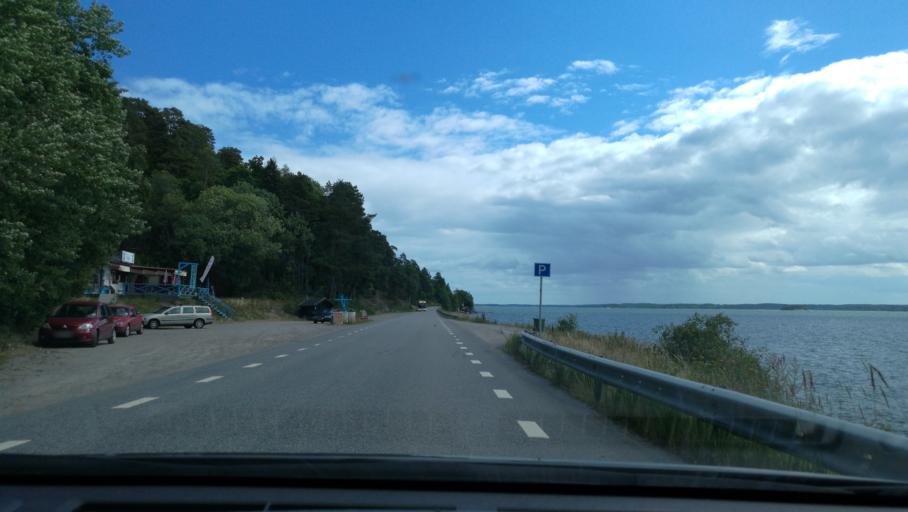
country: SE
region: OEstergoetland
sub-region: Norrkopings Kommun
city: Krokek
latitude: 58.6595
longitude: 16.3793
